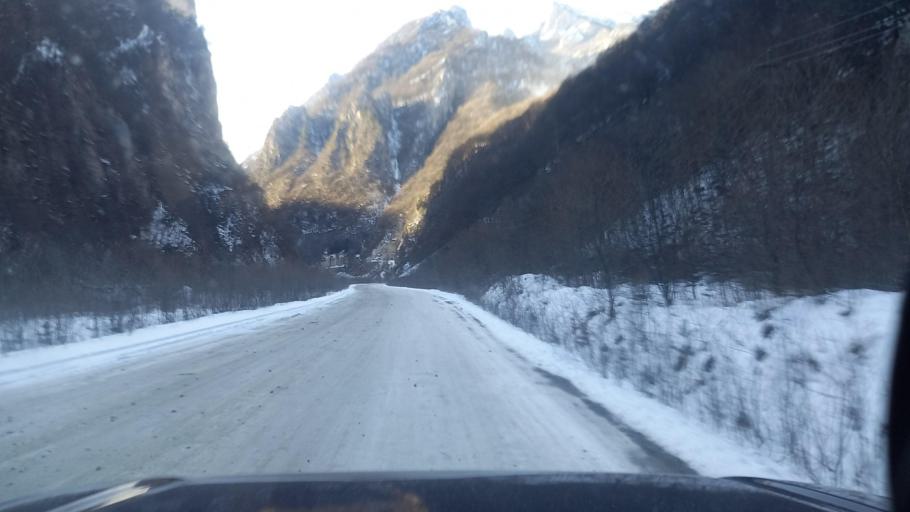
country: RU
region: North Ossetia
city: Gizel'
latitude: 42.8970
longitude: 44.5245
